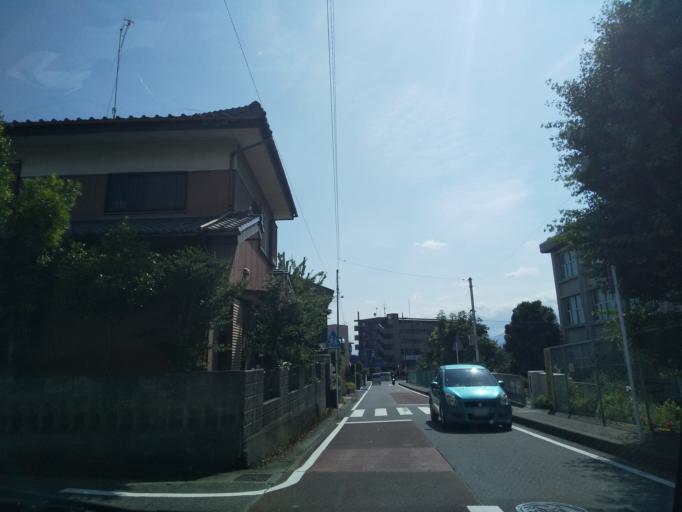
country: JP
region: Kanagawa
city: Minami-rinkan
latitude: 35.4661
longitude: 139.4176
